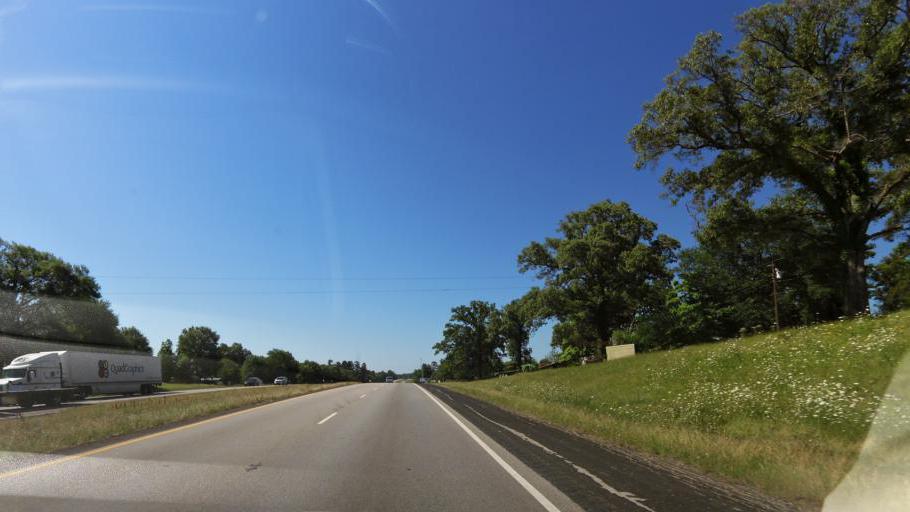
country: US
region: Texas
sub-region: Angelina County
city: Redland
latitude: 31.4445
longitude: -94.7267
